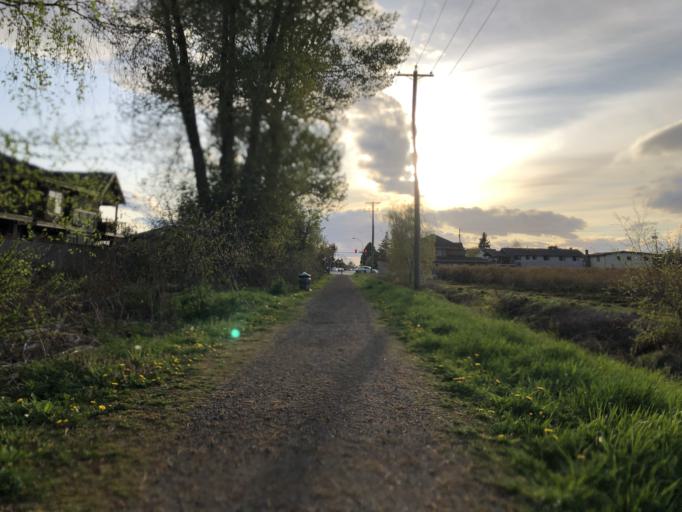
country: CA
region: British Columbia
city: Richmond
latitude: 49.1480
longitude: -123.1116
